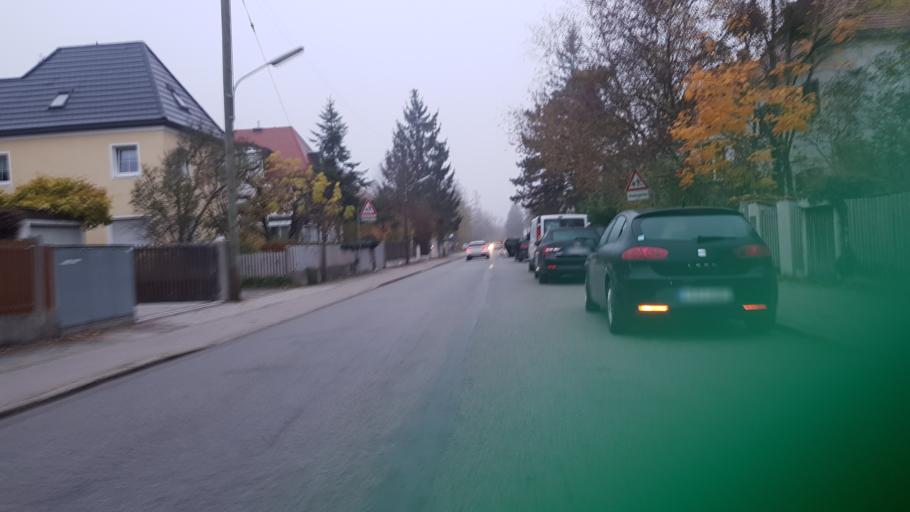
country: DE
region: Bavaria
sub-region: Upper Bavaria
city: Pasing
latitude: 48.1600
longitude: 11.4787
